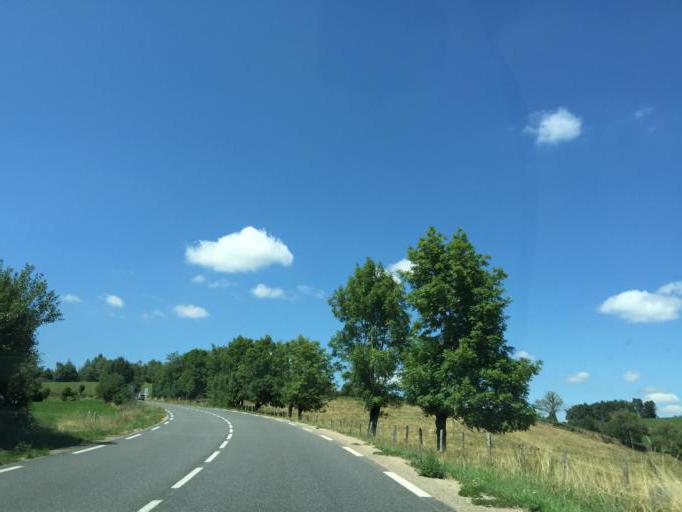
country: FR
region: Midi-Pyrenees
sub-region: Departement de l'Aveyron
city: Espalion
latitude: 44.5804
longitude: 2.7952
